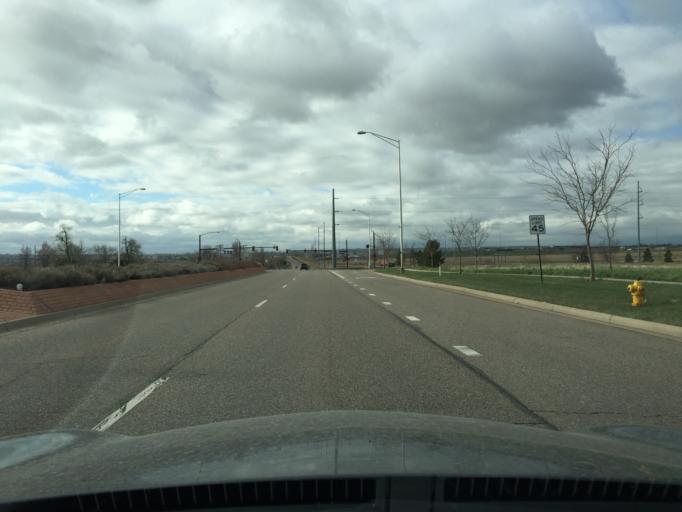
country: US
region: Colorado
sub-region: Boulder County
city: Erie
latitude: 39.9883
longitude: -104.9784
